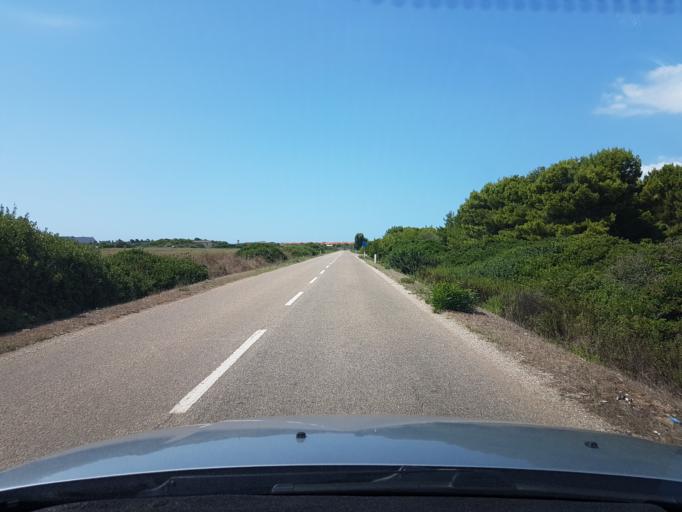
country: IT
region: Sardinia
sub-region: Provincia di Oristano
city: Riola Sardo
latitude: 40.0353
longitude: 8.4218
